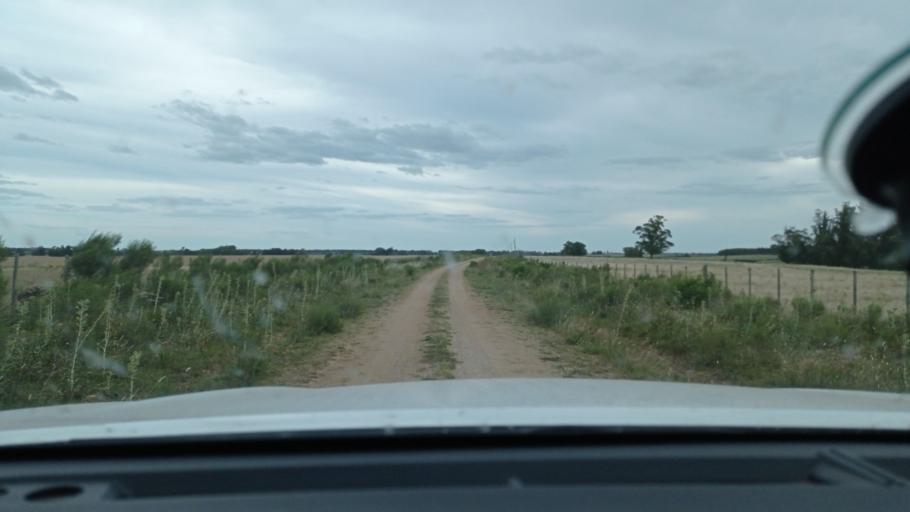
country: UY
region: Florida
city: Casupa
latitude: -34.1344
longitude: -55.8015
